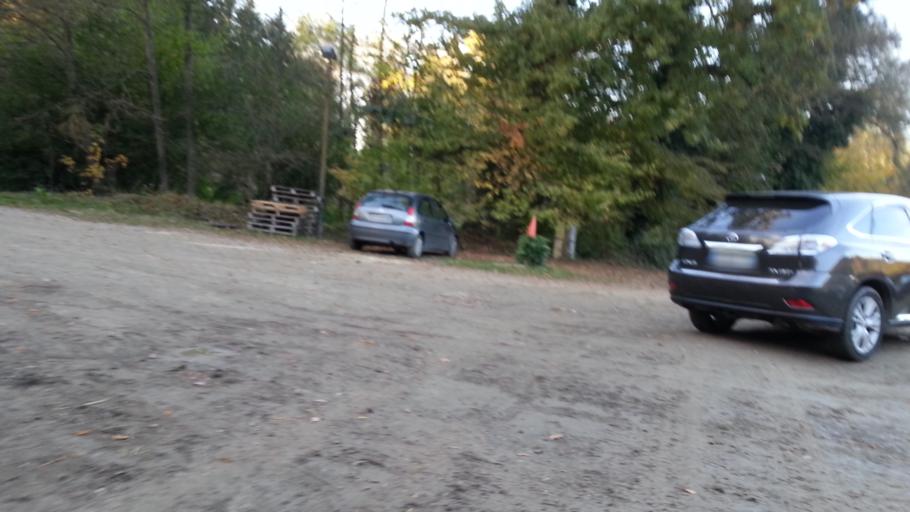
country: FR
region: Picardie
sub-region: Departement de l'Oise
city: Balagny-sur-Therain
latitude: 49.2849
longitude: 2.3472
